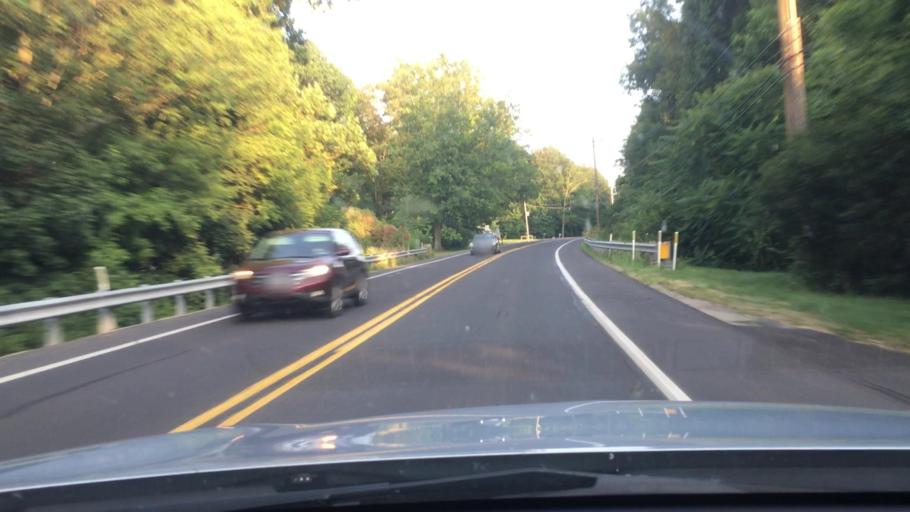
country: US
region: Pennsylvania
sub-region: York County
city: Dover
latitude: 40.0327
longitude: -76.8796
